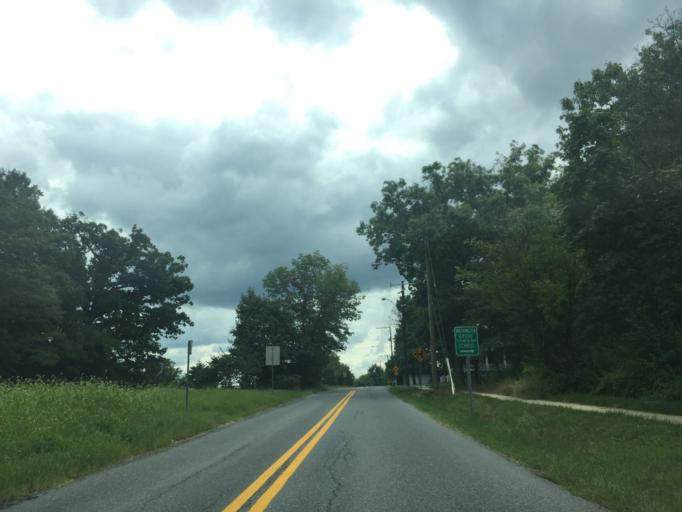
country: US
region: Maryland
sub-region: Montgomery County
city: Derwood
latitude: 39.1355
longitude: -77.1772
